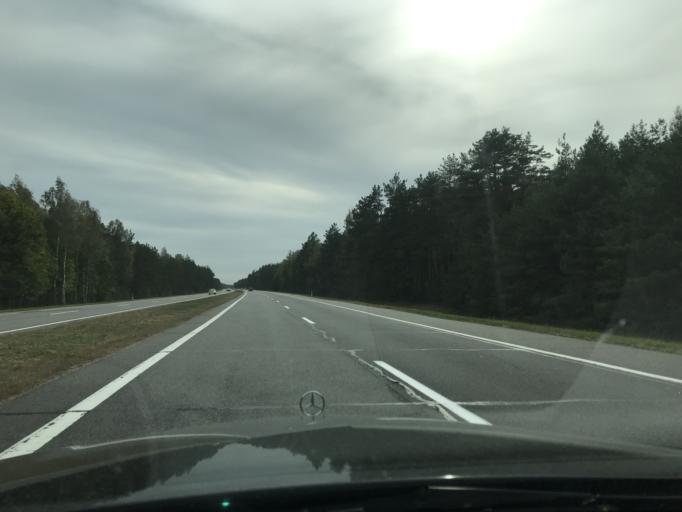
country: BY
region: Brest
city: Baranovichi
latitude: 52.9930
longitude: 25.7576
